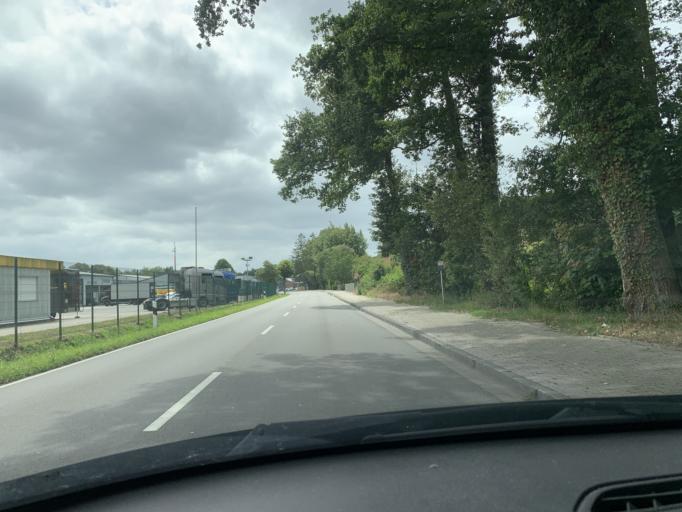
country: DE
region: Lower Saxony
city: Westerstede
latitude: 53.2679
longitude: 7.9378
